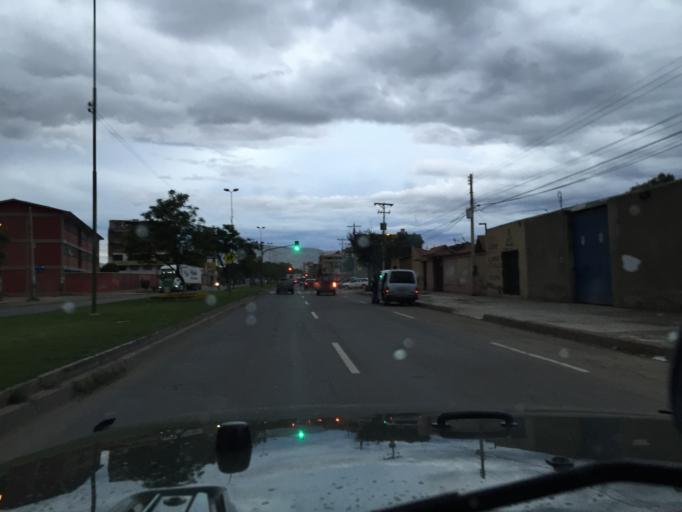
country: BO
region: Cochabamba
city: Cochabamba
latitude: -17.3970
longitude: -66.1819
